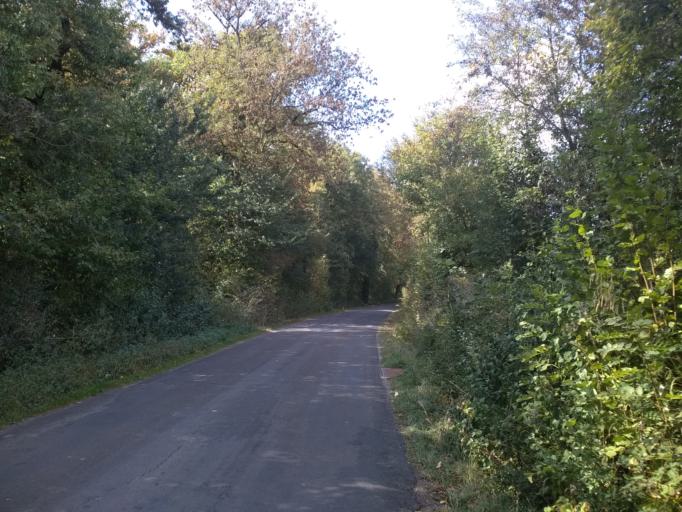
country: FR
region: Midi-Pyrenees
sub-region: Departement de l'Aveyron
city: Bozouls
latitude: 44.4594
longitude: 2.6800
